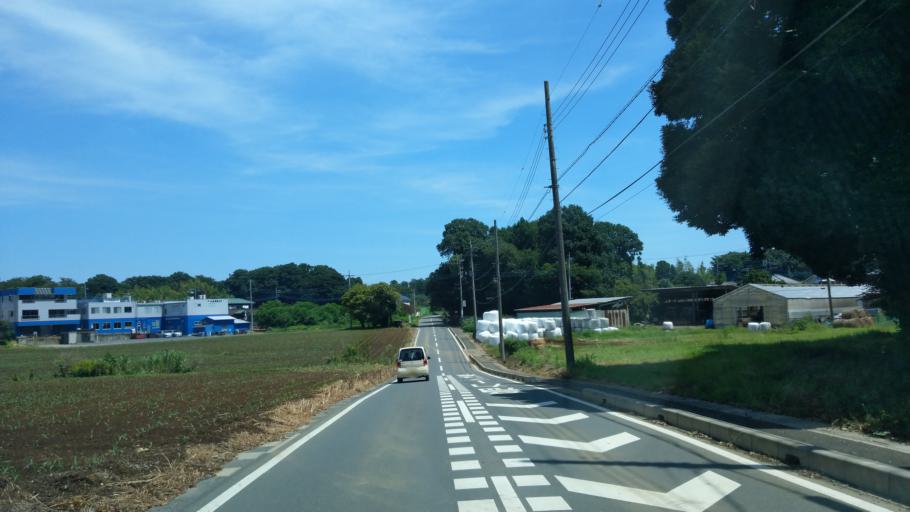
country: JP
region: Saitama
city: Ageoshimo
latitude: 35.9311
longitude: 139.5642
